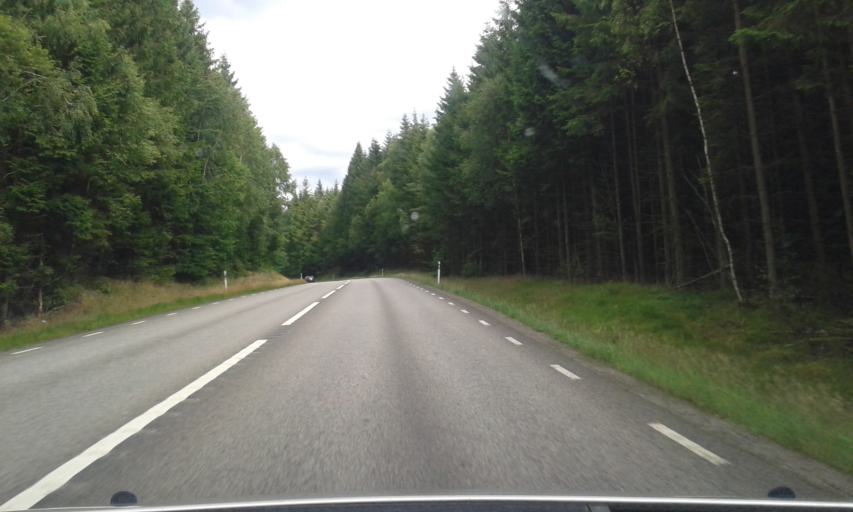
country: SE
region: Vaestra Goetaland
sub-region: Marks Kommun
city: Horred
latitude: 57.1565
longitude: 12.6591
